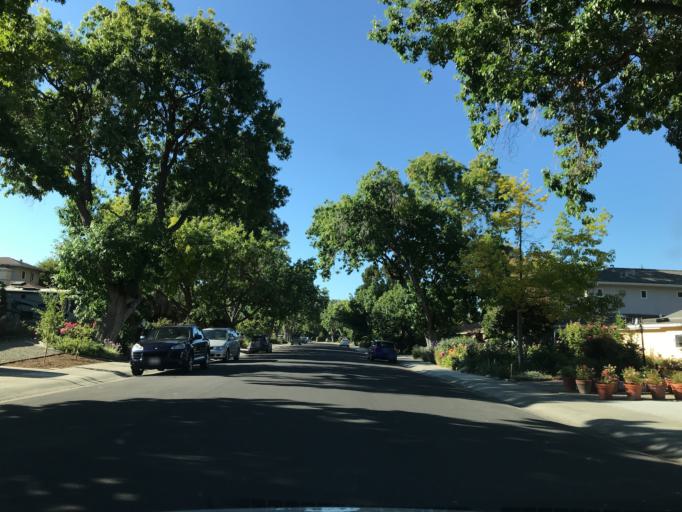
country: US
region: California
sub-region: Santa Clara County
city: Los Altos
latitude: 37.4191
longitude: -122.1051
